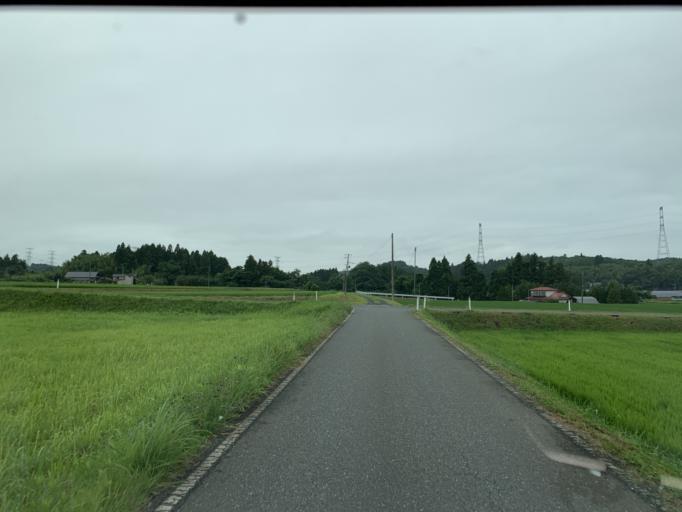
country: JP
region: Iwate
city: Ichinoseki
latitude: 38.8567
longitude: 141.1532
